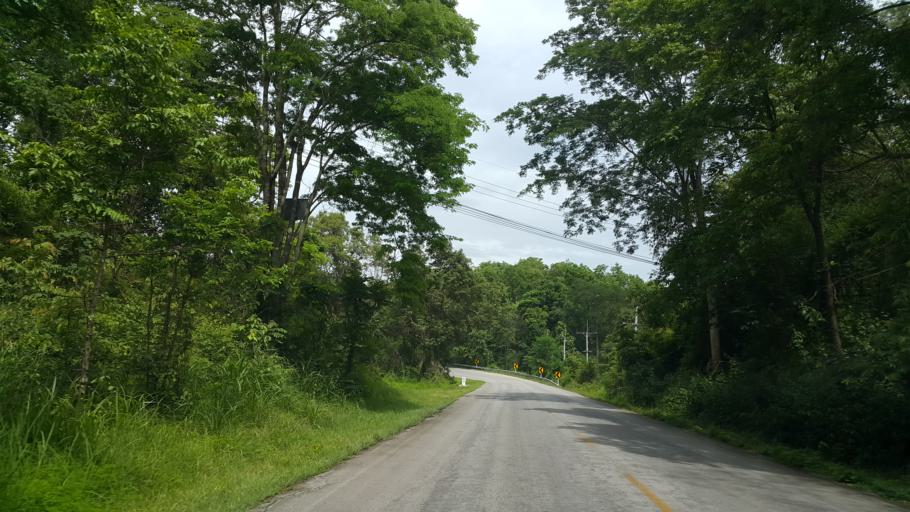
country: TH
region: Lampang
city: Mueang Pan
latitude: 18.7757
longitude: 99.5440
